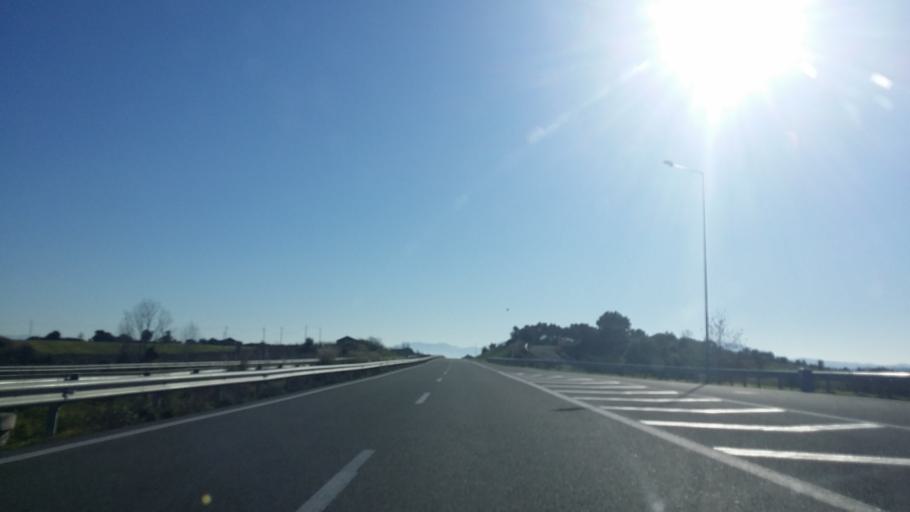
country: GR
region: West Greece
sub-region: Nomos Aitolias kai Akarnanias
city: Fitiai
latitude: 38.6733
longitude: 21.2256
